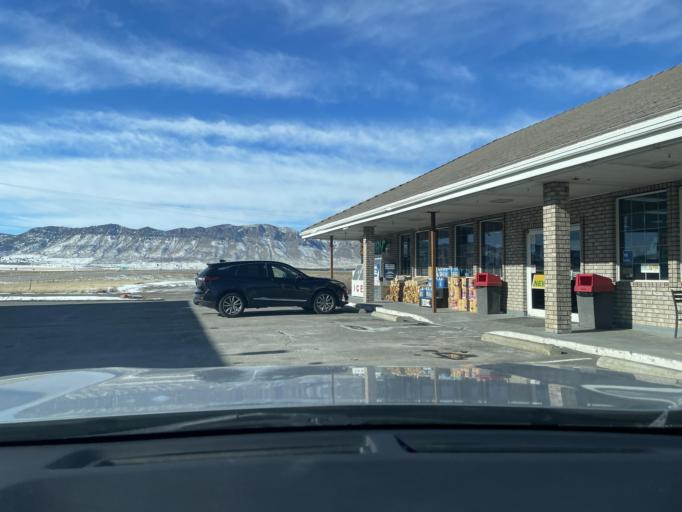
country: US
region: Utah
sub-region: Sanpete County
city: Gunnison
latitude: 39.2520
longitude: -112.1096
